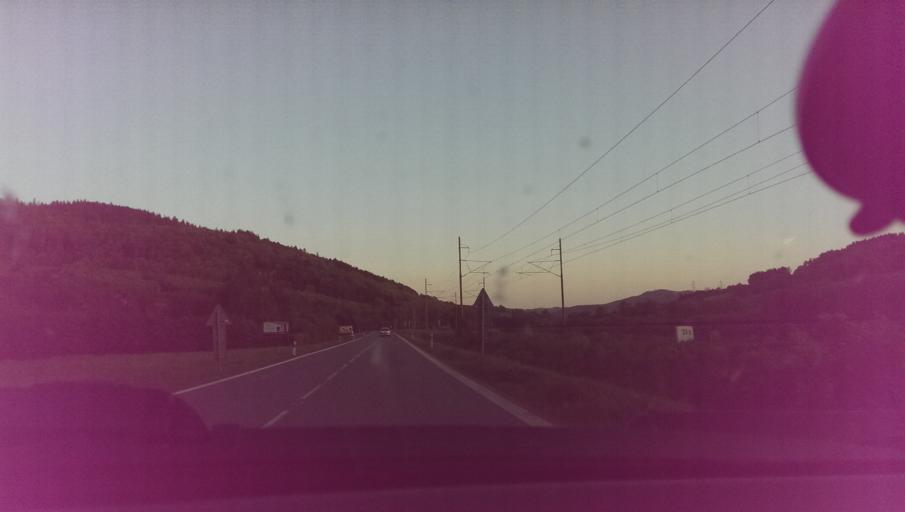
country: CZ
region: Zlin
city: Jablunka
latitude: 49.4123
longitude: 17.9524
